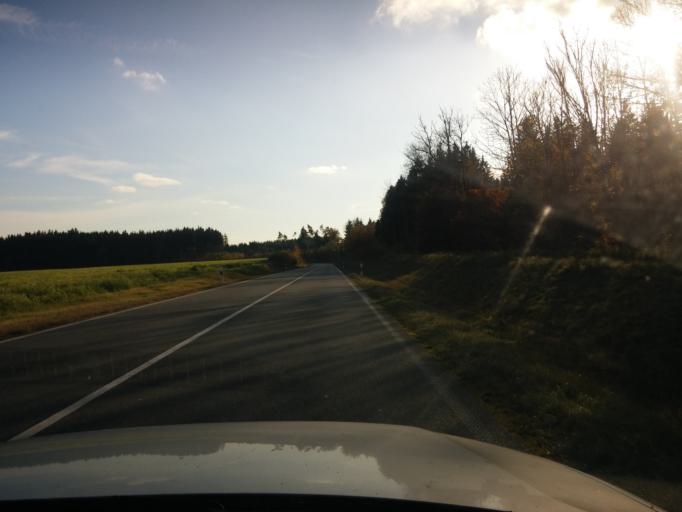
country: DE
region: Bavaria
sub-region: Upper Bavaria
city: Brunnthal
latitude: 48.0241
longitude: 11.6955
